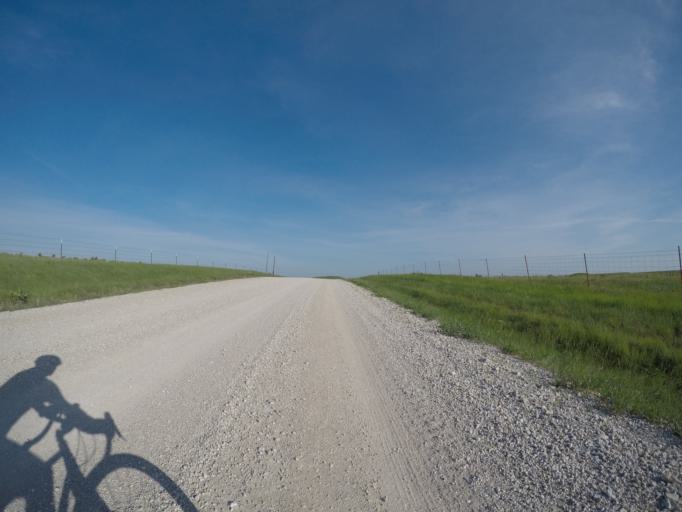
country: US
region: Kansas
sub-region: Riley County
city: Manhattan
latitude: 39.0489
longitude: -96.4943
